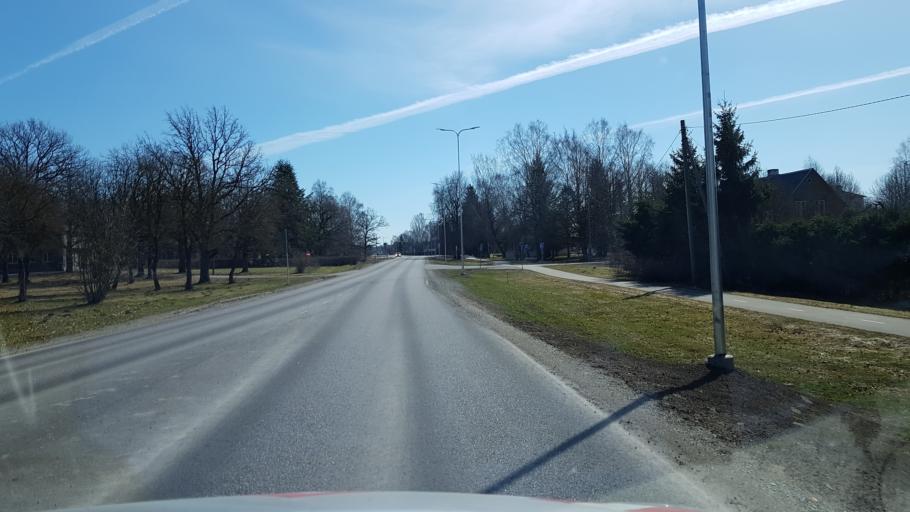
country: EE
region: Laeaene-Virumaa
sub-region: Vinni vald
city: Vinni
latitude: 59.2839
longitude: 26.4126
